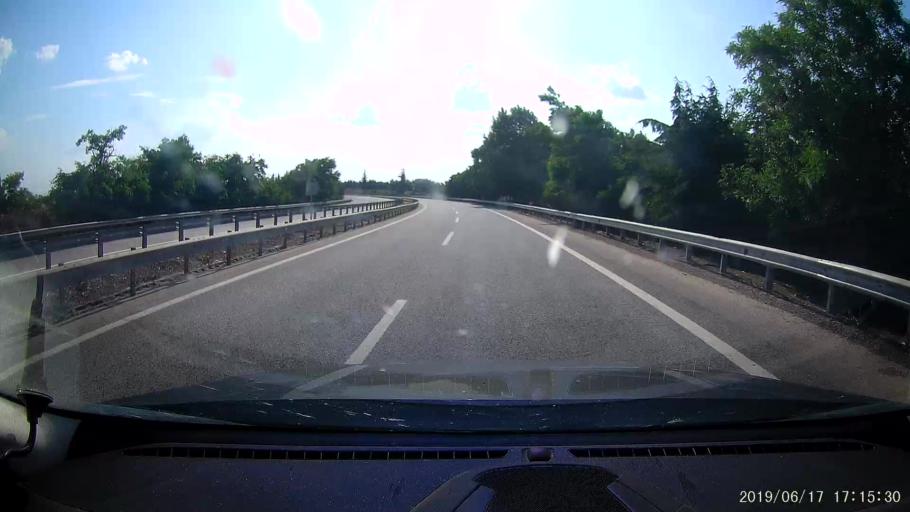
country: GR
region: East Macedonia and Thrace
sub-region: Nomos Evrou
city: Kastanies
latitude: 41.7021
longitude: 26.4949
